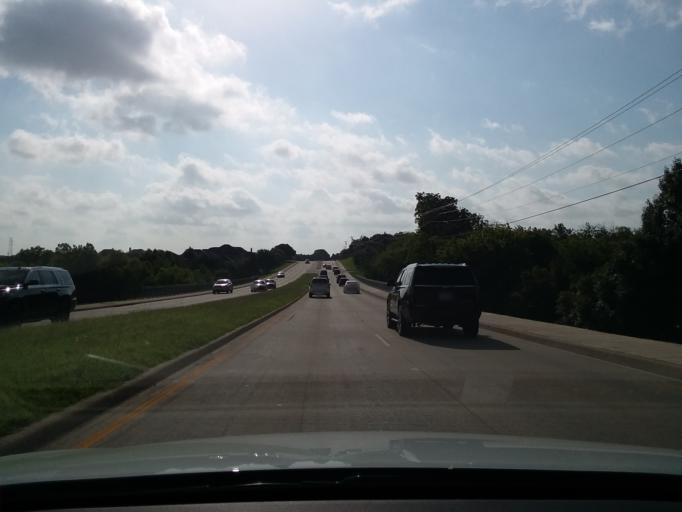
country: US
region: Texas
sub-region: Denton County
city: Bartonville
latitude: 33.0739
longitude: -97.1218
